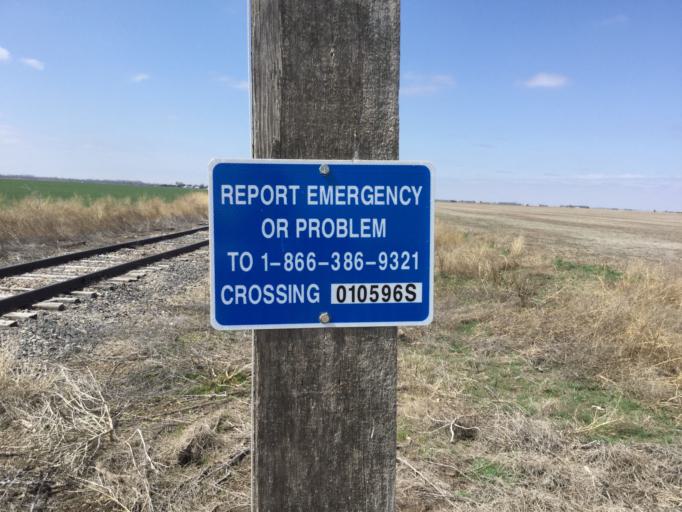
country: US
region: Kansas
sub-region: Barton County
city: Ellinwood
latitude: 38.3520
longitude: -98.4986
